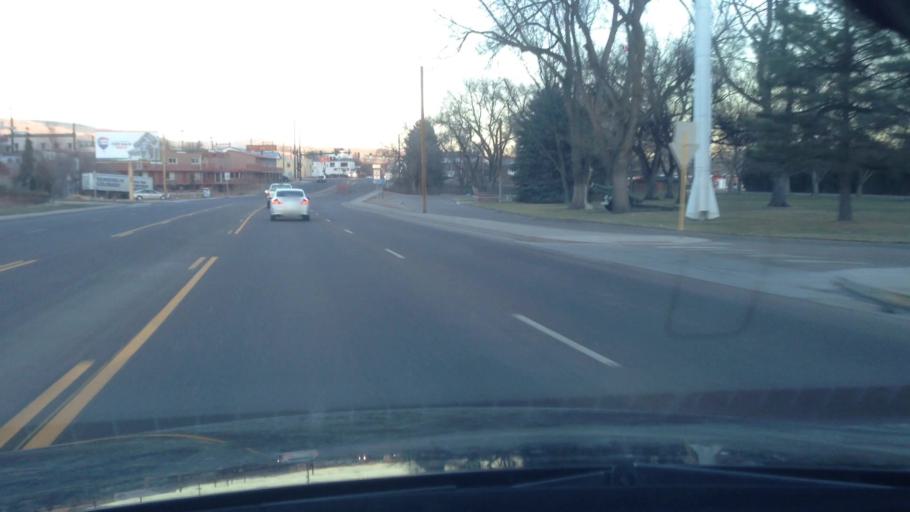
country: US
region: Colorado
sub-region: Fremont County
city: Canon City
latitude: 38.4372
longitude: -105.2449
